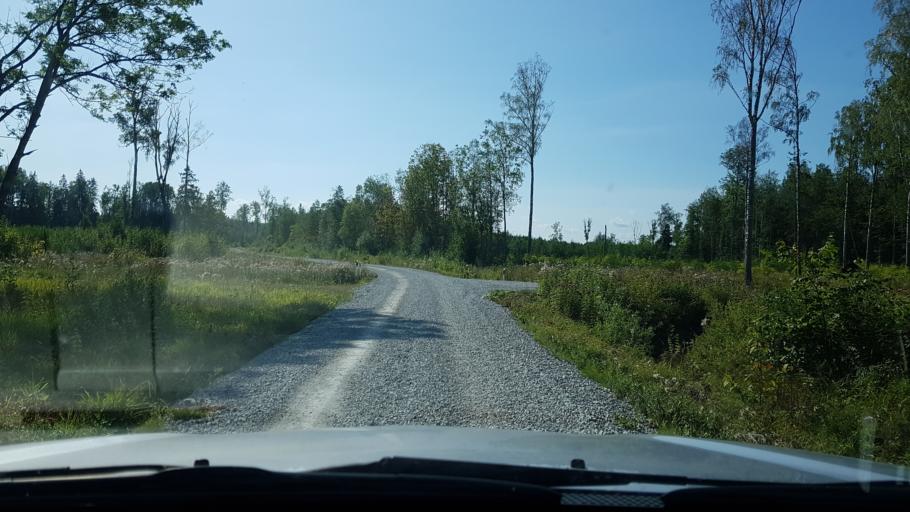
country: EE
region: Ida-Virumaa
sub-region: Sillamaee linn
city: Sillamae
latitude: 59.3365
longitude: 27.7329
